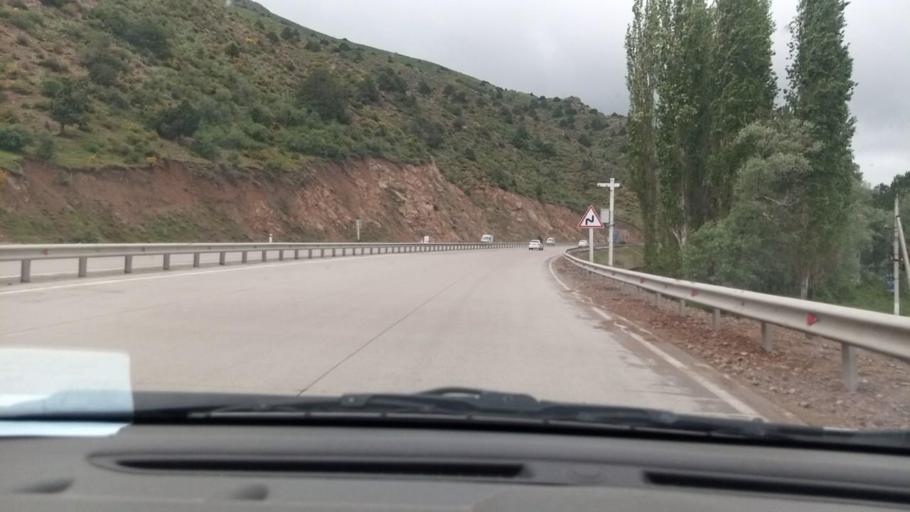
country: TJ
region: Viloyati Sughd
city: Shaydon
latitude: 41.0343
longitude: 70.5851
